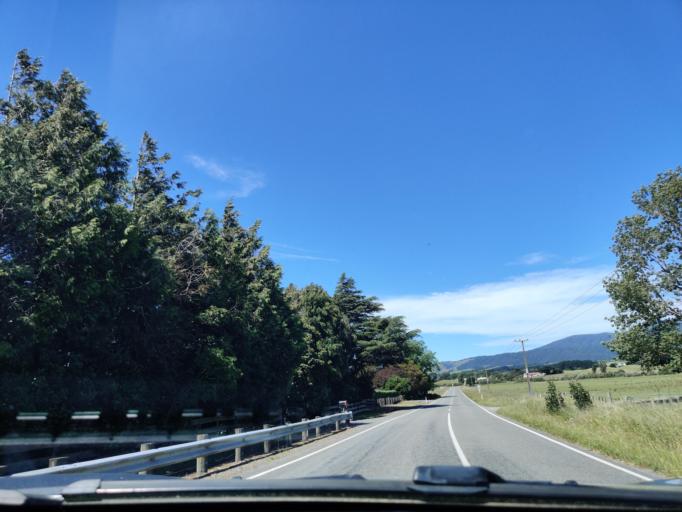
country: NZ
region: Wellington
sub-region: Upper Hutt City
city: Upper Hutt
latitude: -41.3283
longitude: 175.2126
